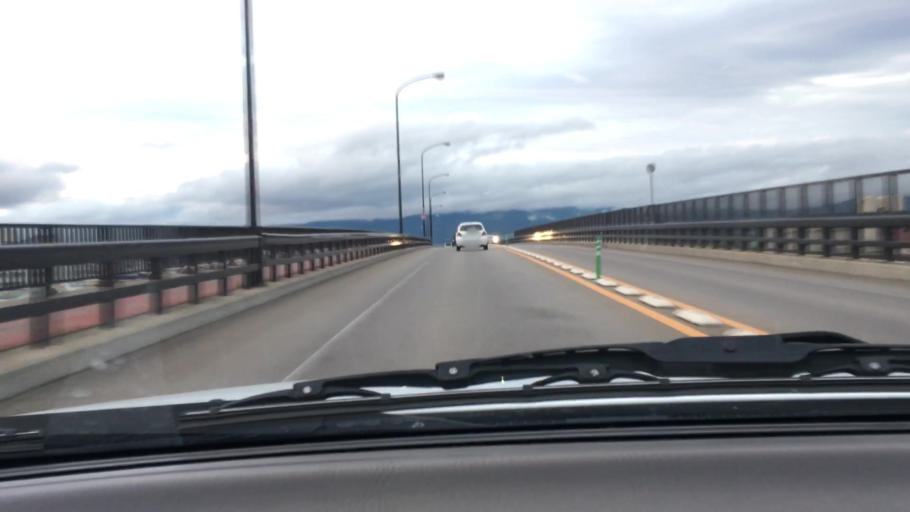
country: JP
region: Hokkaido
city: Hakodate
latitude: 41.7794
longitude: 140.7261
